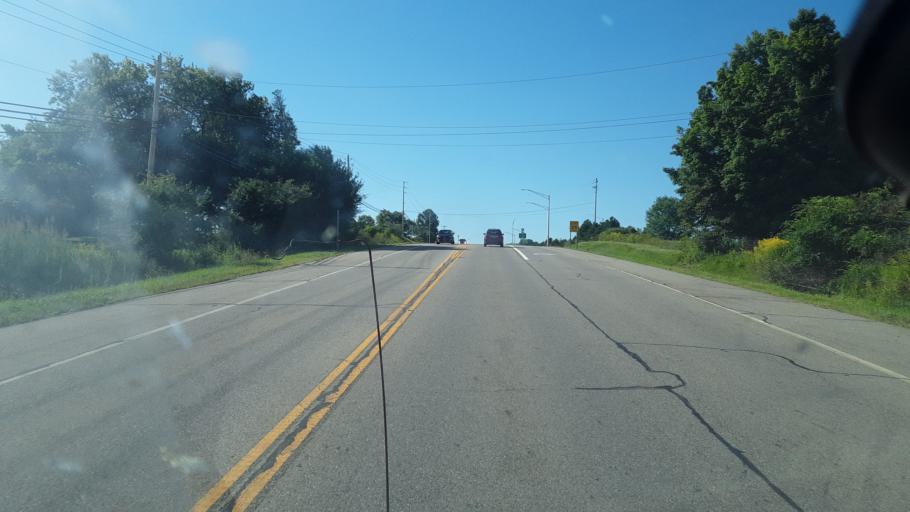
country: US
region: Ohio
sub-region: Portage County
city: Mantua
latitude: 41.2488
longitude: -81.2312
